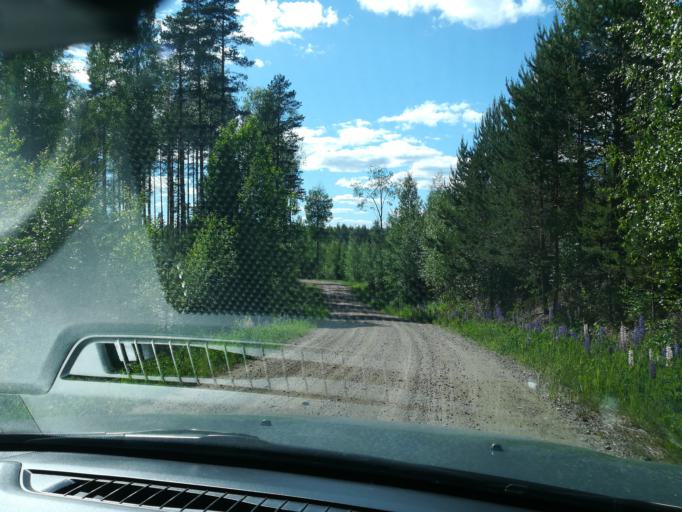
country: FI
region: Southern Savonia
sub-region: Mikkeli
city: Puumala
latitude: 61.6601
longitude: 28.1597
